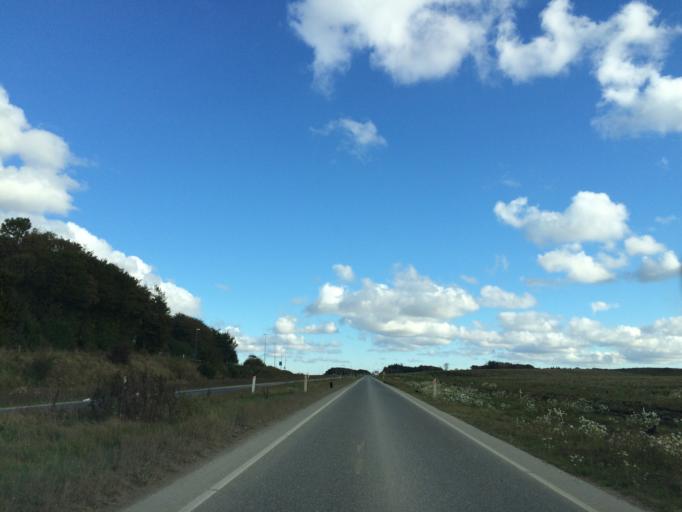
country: DK
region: Central Jutland
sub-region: Skanderborg Kommune
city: Ry
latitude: 56.1486
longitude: 9.7855
